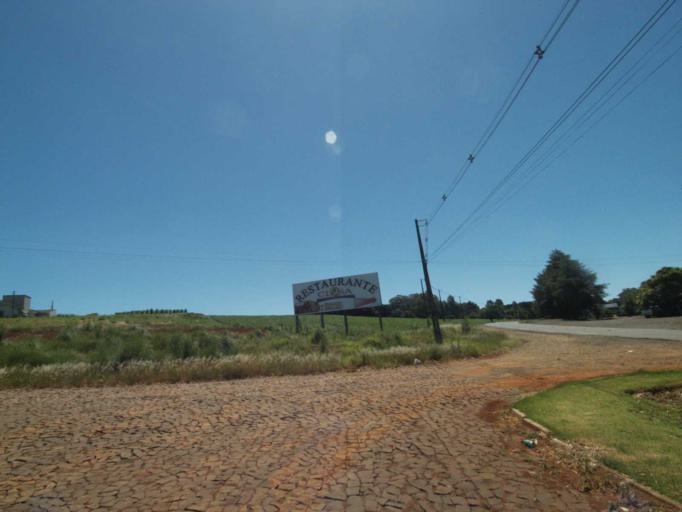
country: BR
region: Parana
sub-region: Coronel Vivida
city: Coronel Vivida
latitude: -25.9790
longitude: -52.8168
